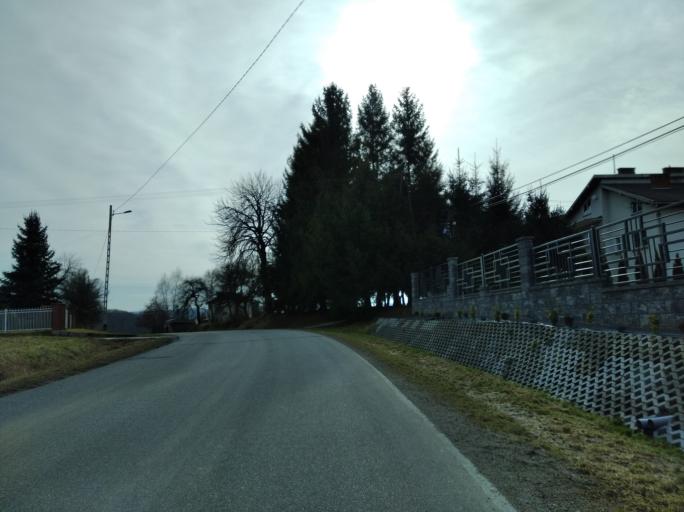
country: PL
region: Subcarpathian Voivodeship
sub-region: Powiat brzozowski
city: Orzechowka
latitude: 49.7375
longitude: 21.9417
